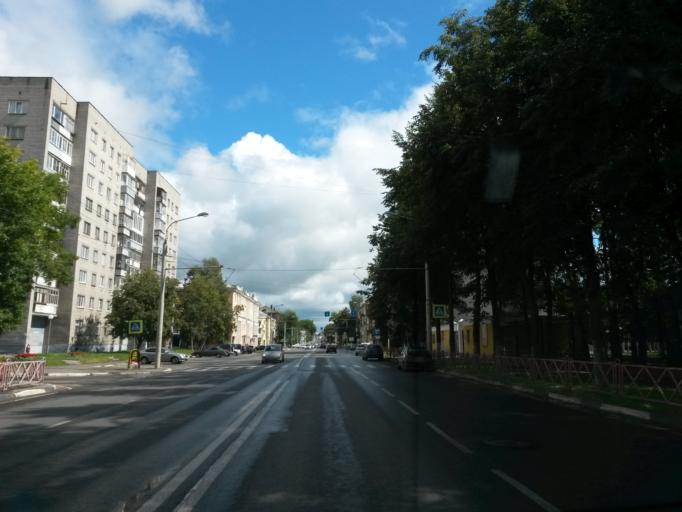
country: RU
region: Jaroslavl
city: Yaroslavl
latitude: 57.6213
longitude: 39.8649
